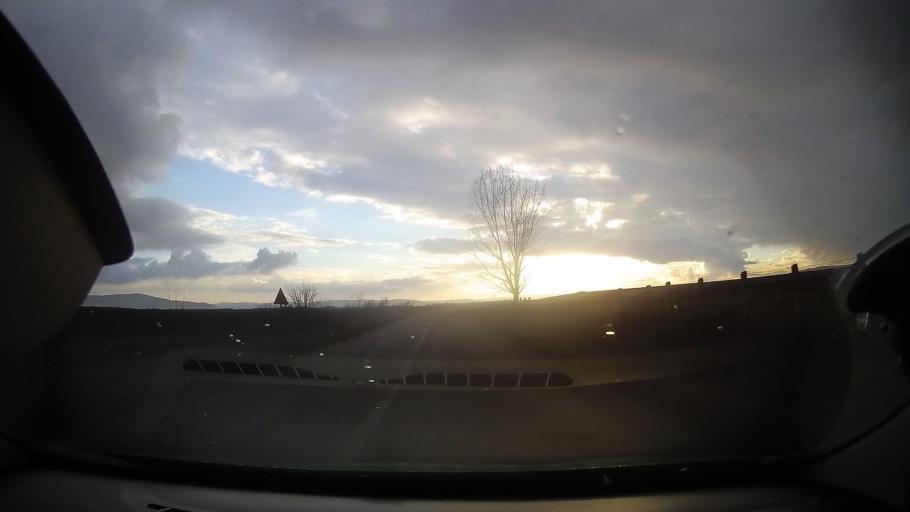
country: RO
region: Alba
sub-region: Comuna Lunca Muresului
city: Lunca Muresului
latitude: 46.4490
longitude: 23.9183
